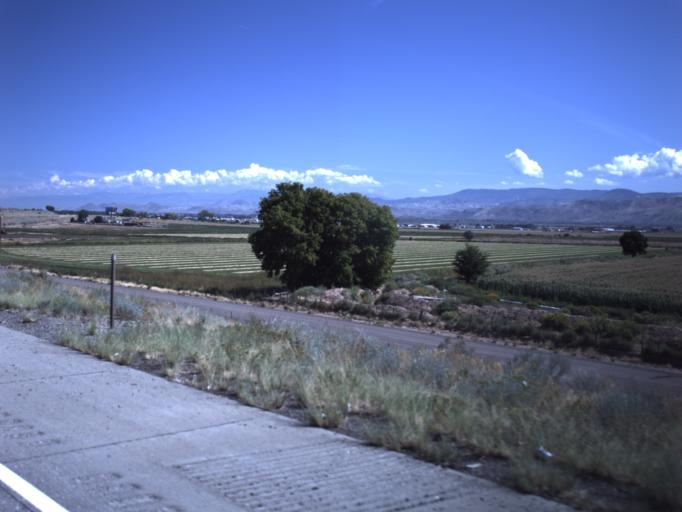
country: US
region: Utah
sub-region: Sevier County
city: Richfield
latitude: 38.7236
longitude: -112.1304
